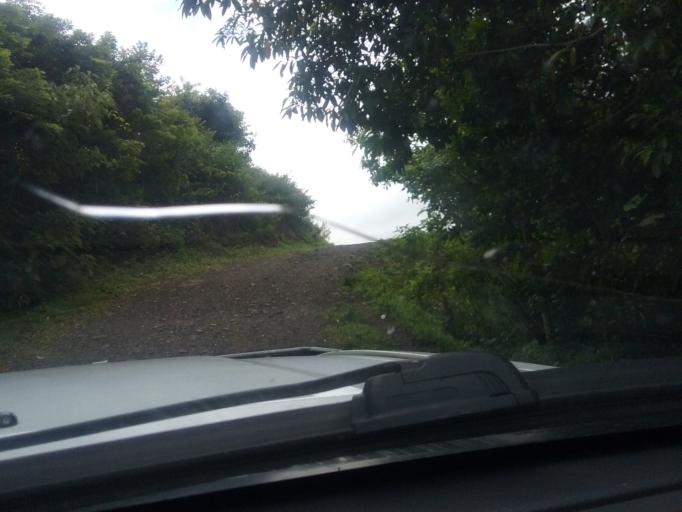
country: NI
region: Matagalpa
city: Matagalpa
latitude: 12.8702
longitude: -85.9316
